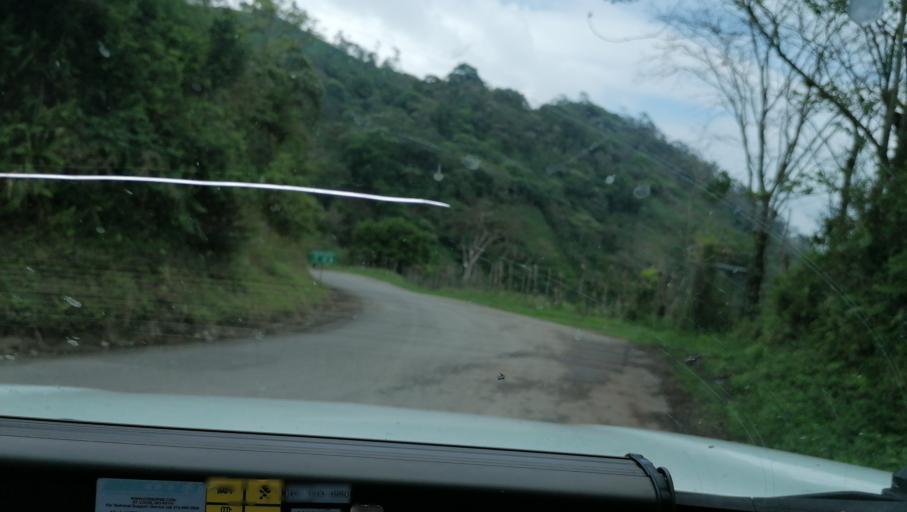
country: MX
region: Chiapas
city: Ocotepec
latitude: 17.3279
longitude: -93.1328
